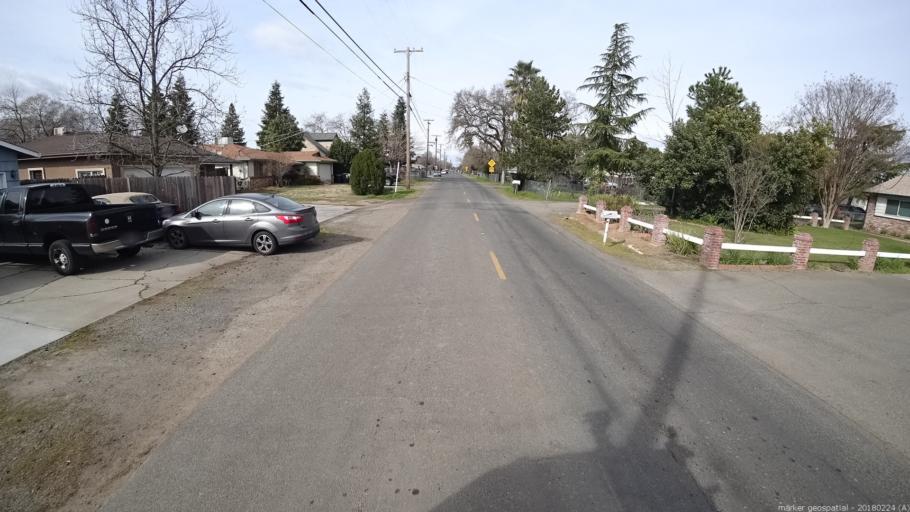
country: US
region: California
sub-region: Sacramento County
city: Rio Linda
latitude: 38.6988
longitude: -121.4430
